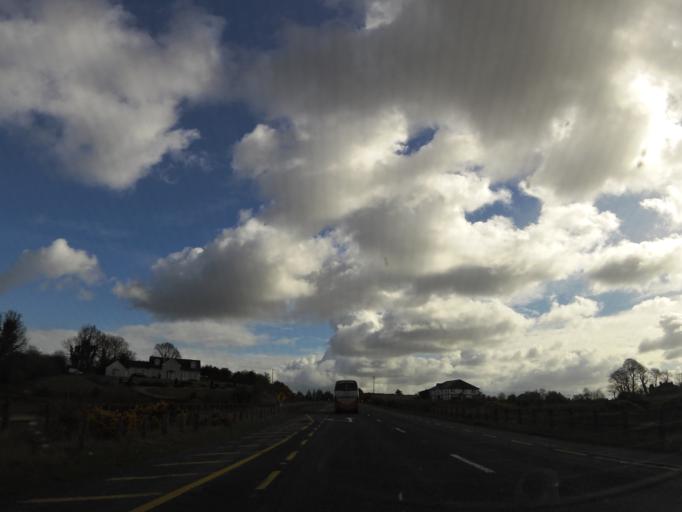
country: IE
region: Connaught
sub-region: Maigh Eo
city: Ballyhaunis
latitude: 53.8284
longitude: -8.8731
